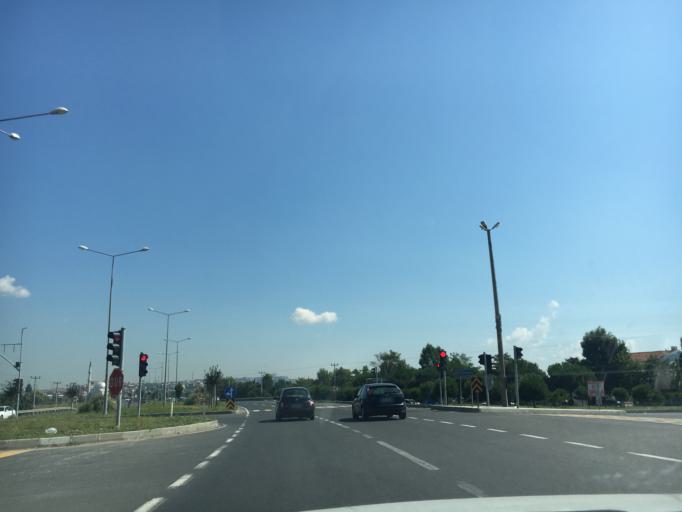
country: TR
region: Tekirdag
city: Sultankoy
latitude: 41.0084
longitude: 27.9805
